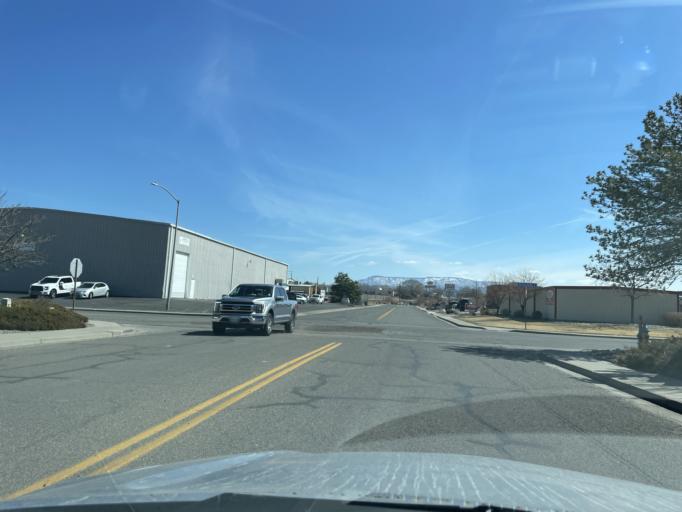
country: US
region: Colorado
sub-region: Mesa County
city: Grand Junction
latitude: 39.0729
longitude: -108.5776
